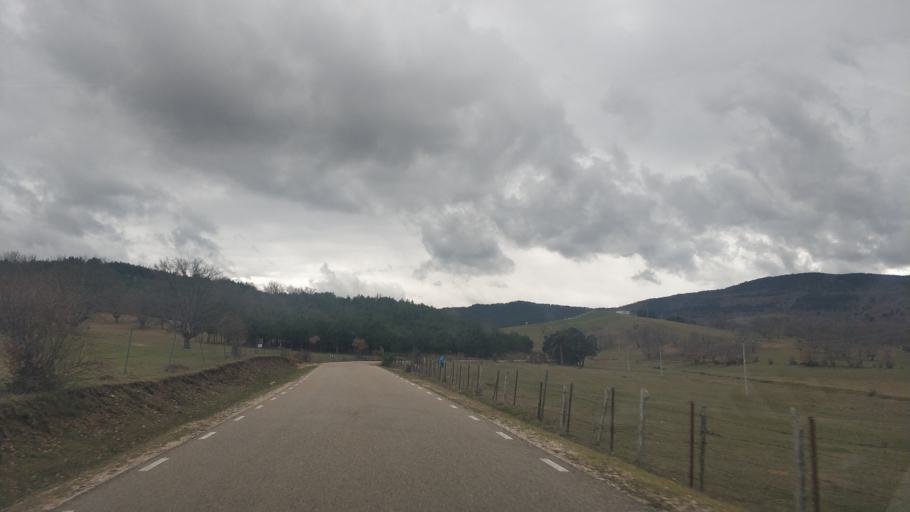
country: ES
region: Castille and Leon
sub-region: Provincia de Burgos
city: Canicosa de la Sierra
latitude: 41.9473
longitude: -3.0318
